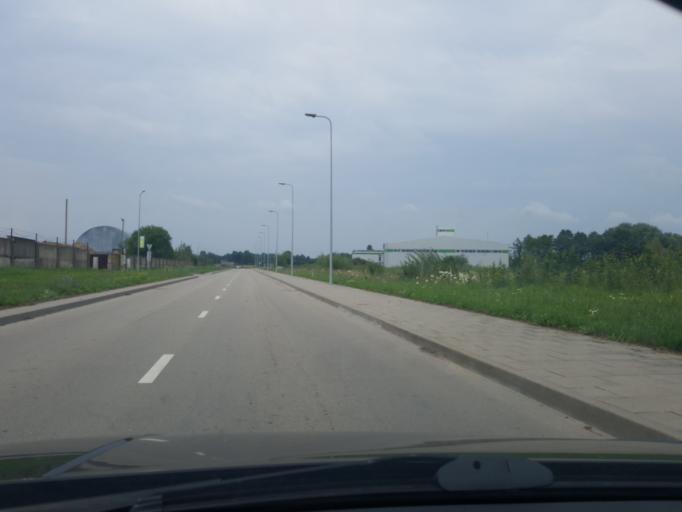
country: LT
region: Alytaus apskritis
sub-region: Alytus
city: Alytus
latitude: 54.4346
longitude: 24.0269
